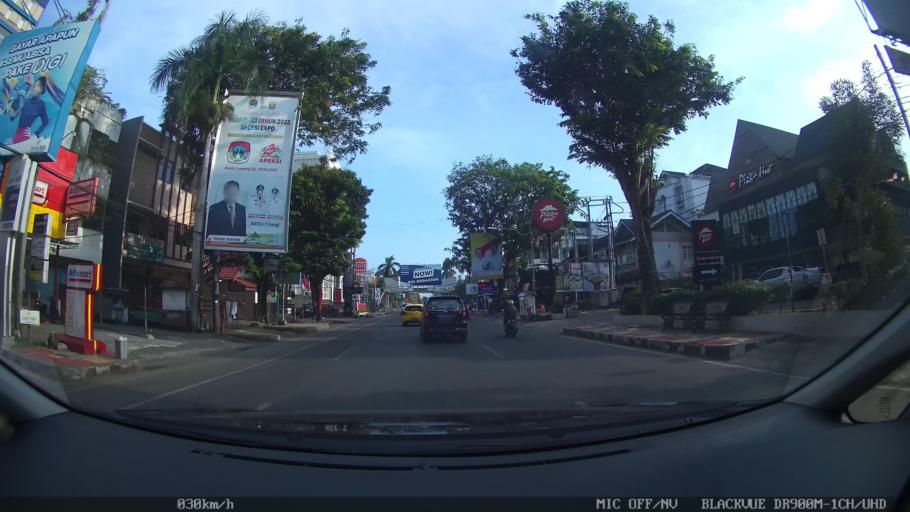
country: ID
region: Lampung
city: Bandarlampung
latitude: -5.4190
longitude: 105.2582
